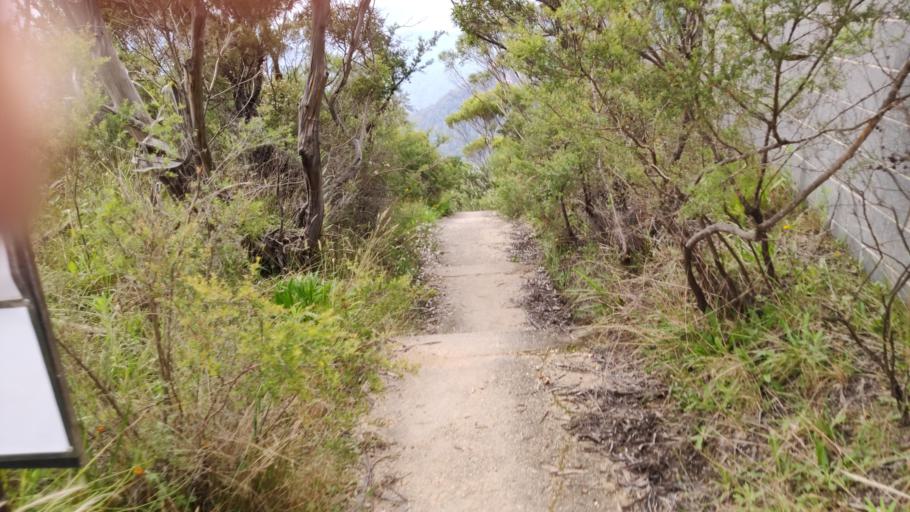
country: AU
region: New South Wales
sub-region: Blue Mountains Municipality
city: Leura
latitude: -33.7251
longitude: 150.3289
